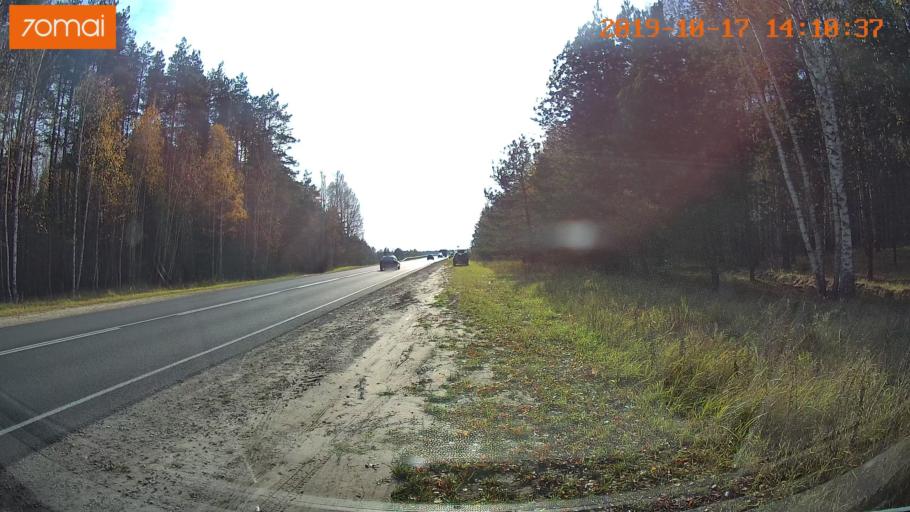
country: RU
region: Rjazan
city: Spas-Klepiki
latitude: 55.0787
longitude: 40.0501
